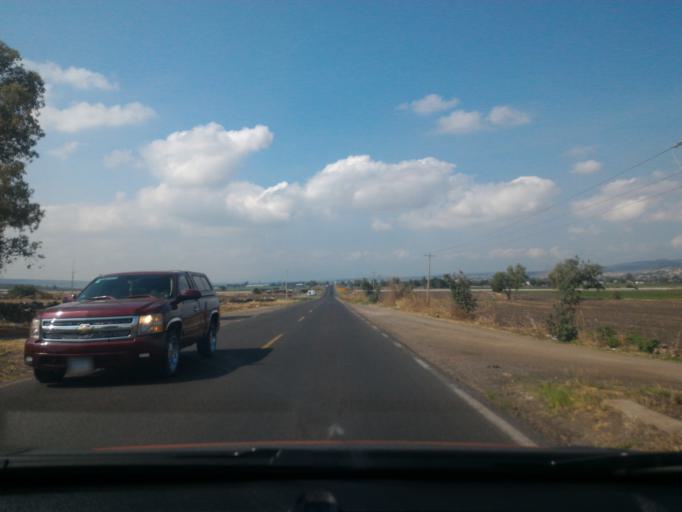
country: MX
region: Guanajuato
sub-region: Penjamo
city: Estacion la Piedad
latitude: 20.4032
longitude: -101.9988
